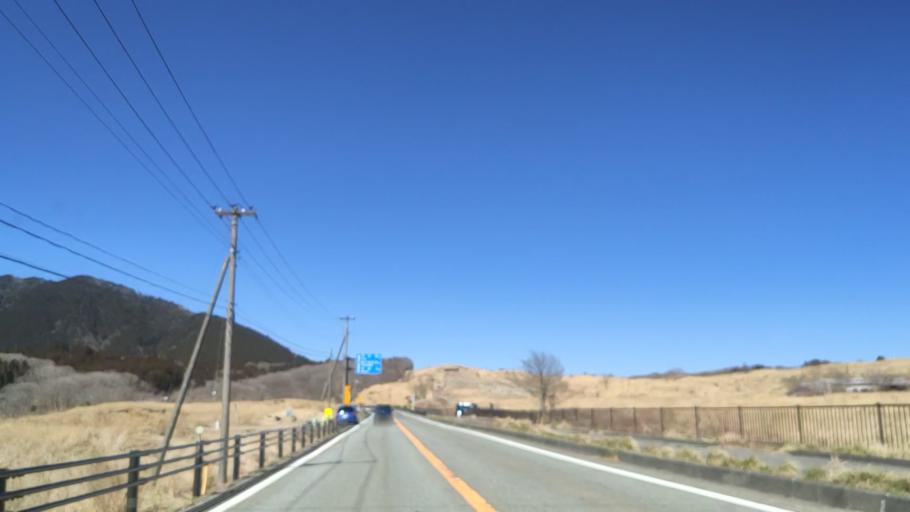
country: JP
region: Yamanashi
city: Fujikawaguchiko
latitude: 35.4223
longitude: 138.5920
